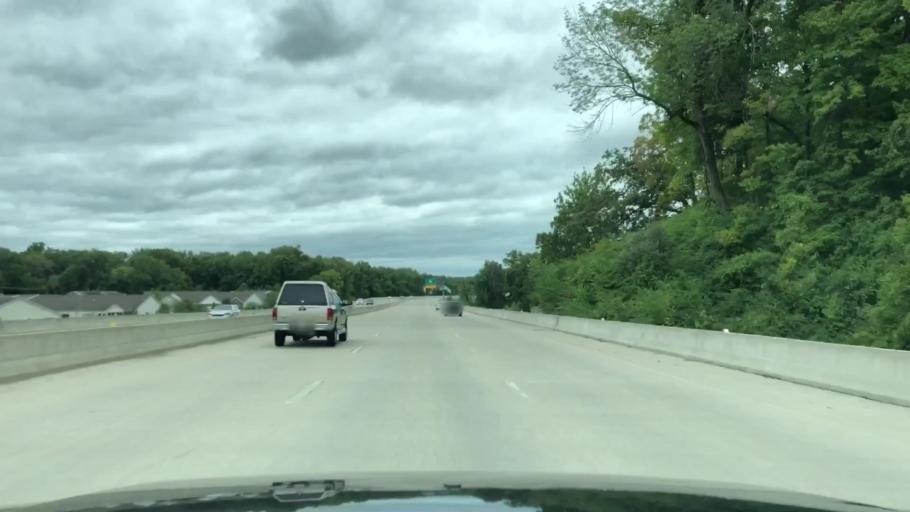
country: US
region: Missouri
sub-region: Saint Louis County
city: Maryland Heights
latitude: 38.6923
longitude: -90.4991
